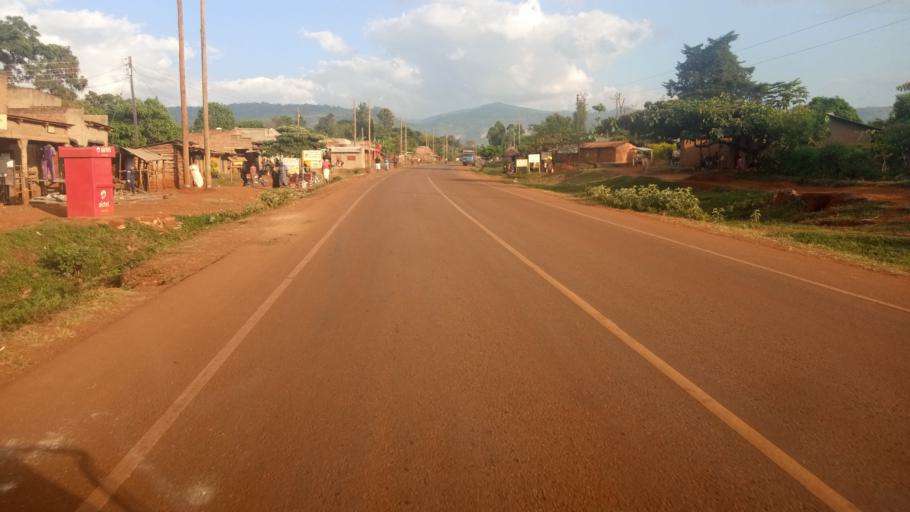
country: UG
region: Eastern Region
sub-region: Sironko District
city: Sironko
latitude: 1.3217
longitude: 34.3357
